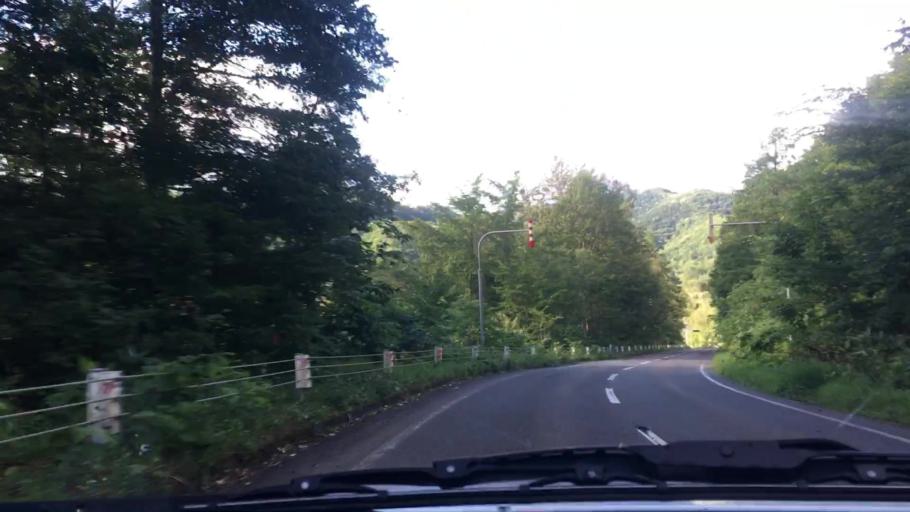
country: JP
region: Hokkaido
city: Otofuke
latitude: 43.1790
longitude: 142.9292
